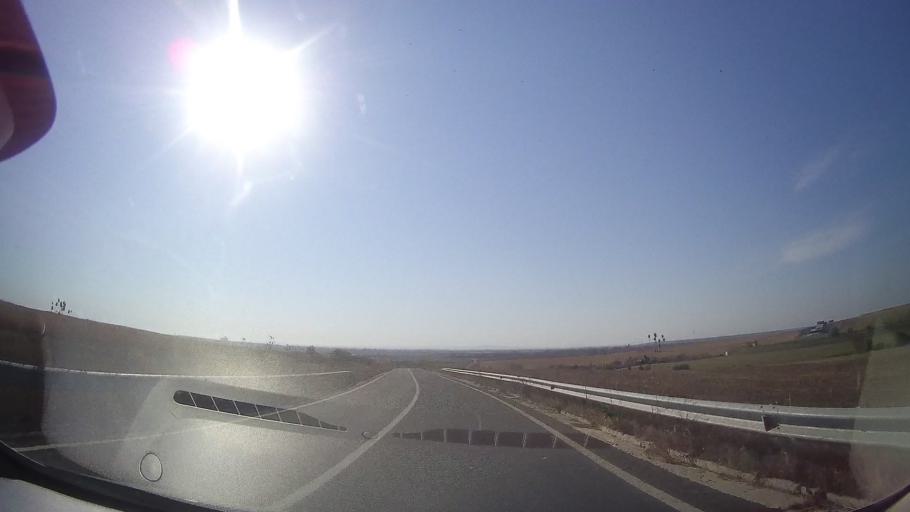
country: RO
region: Timis
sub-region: Comuna Topolovatu Mare
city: Topolovatu Mare
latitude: 45.8044
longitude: 21.5847
